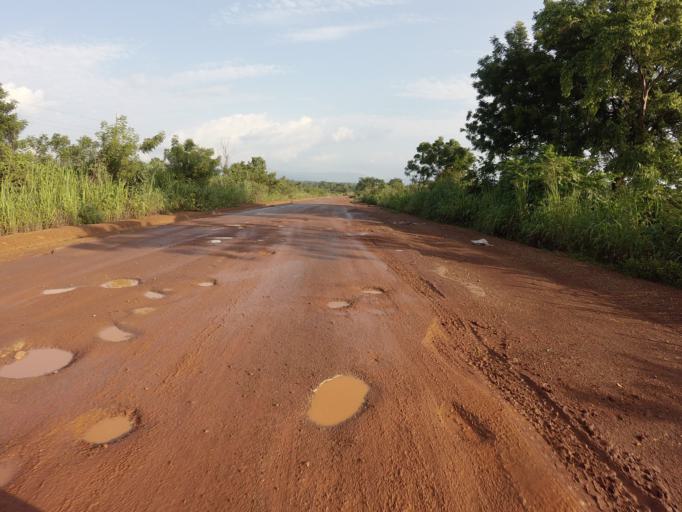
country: GH
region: Volta
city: Kpandu
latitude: 7.0179
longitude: 0.4282
